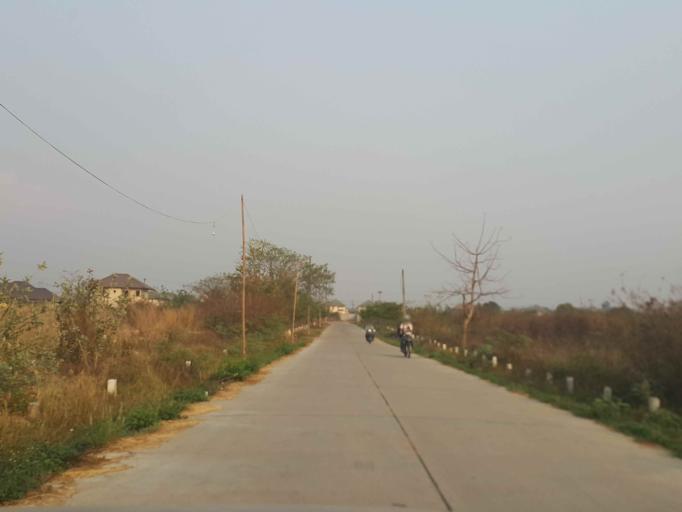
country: TH
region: Chiang Mai
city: San Kamphaeng
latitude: 18.7795
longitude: 99.0705
